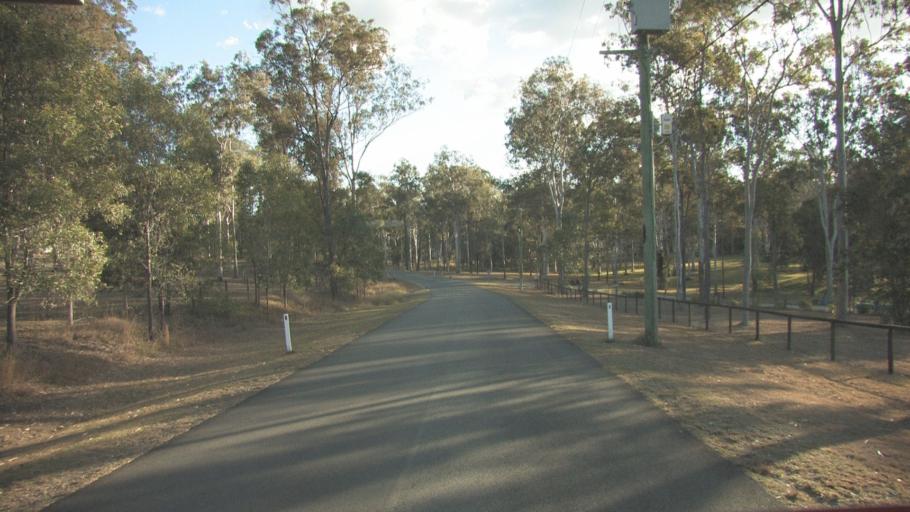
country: AU
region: Queensland
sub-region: Logan
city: Cedar Vale
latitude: -27.8538
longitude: 153.0964
